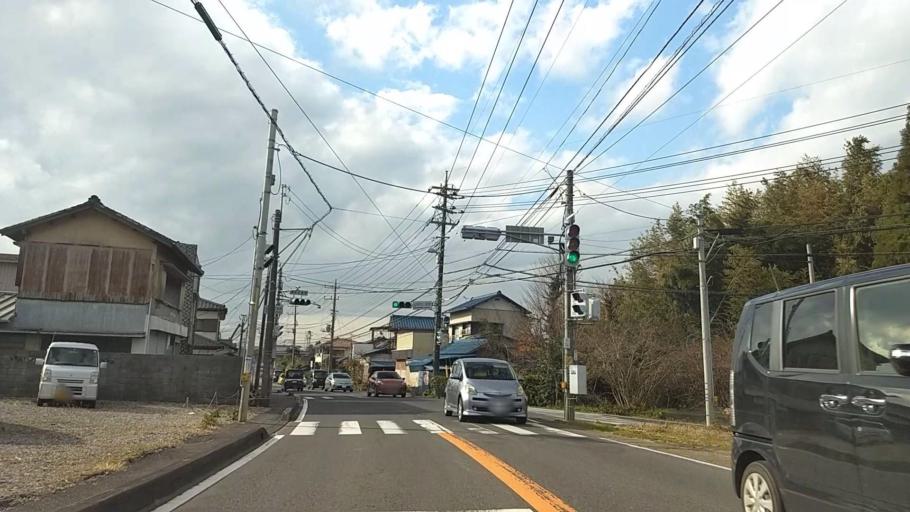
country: JP
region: Chiba
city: Oami
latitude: 35.5756
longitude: 140.2981
